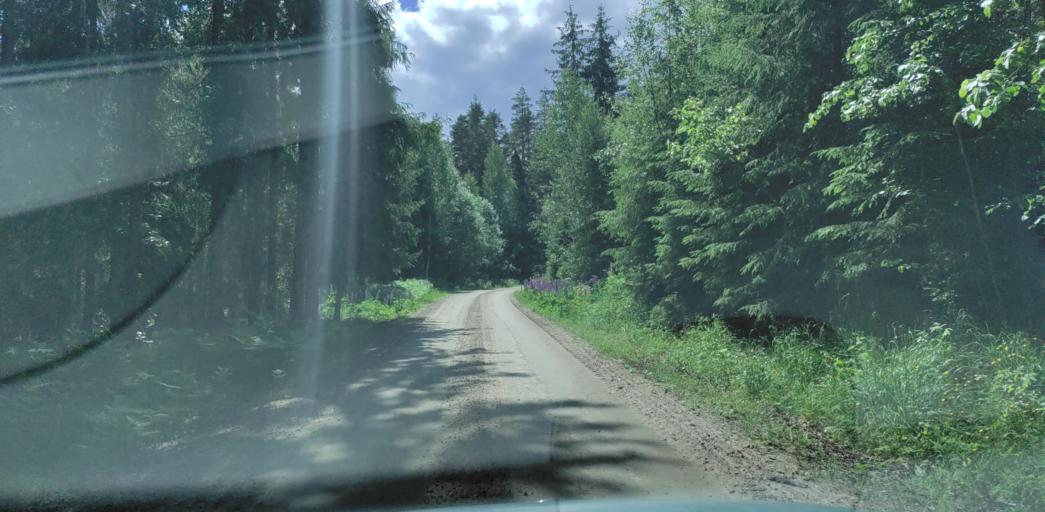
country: SE
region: Vaermland
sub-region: Sunne Kommun
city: Sunne
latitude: 60.0416
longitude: 13.2521
